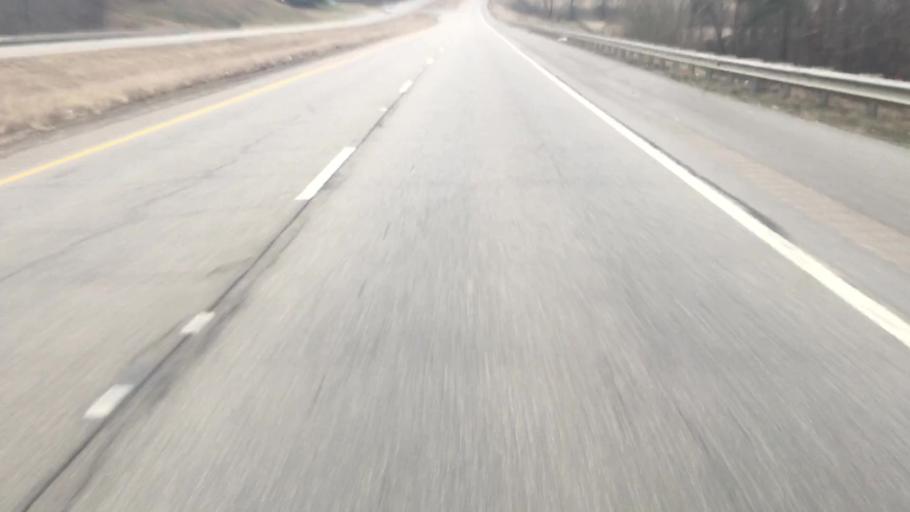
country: US
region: Alabama
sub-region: Walker County
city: Sumiton
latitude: 33.7944
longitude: -87.1040
